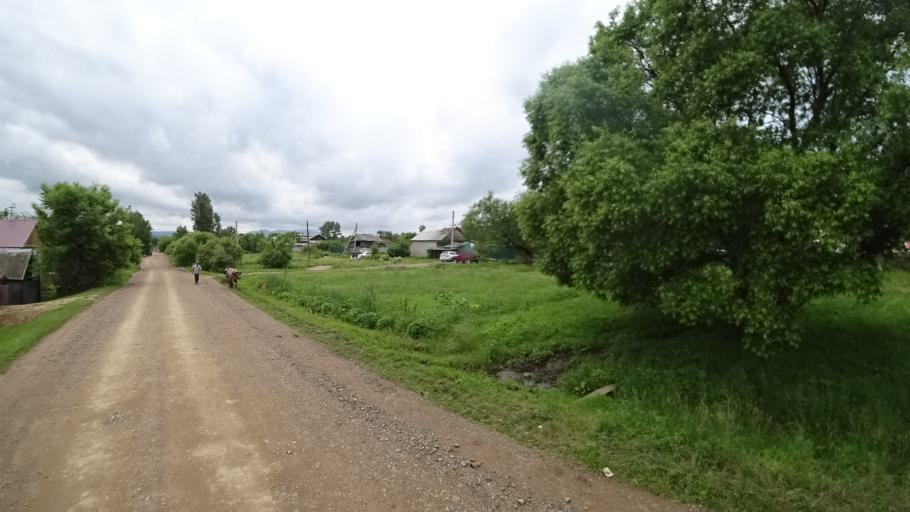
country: RU
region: Primorskiy
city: Novosysoyevka
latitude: 44.2295
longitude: 133.3667
